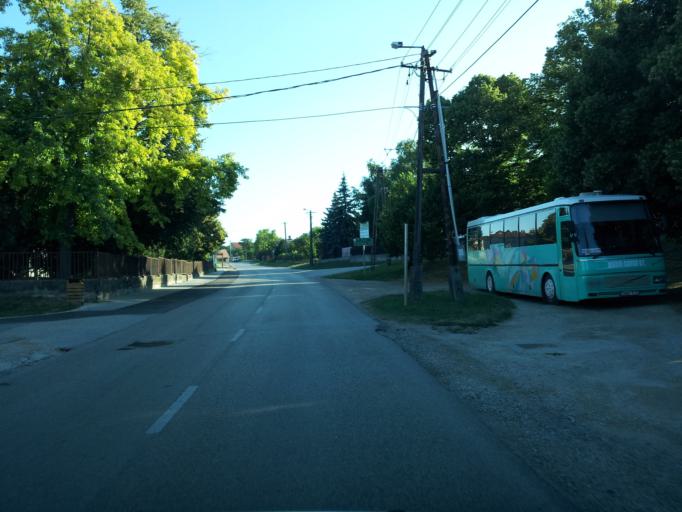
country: HU
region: Fejer
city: Lepseny
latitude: 47.0221
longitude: 18.2128
